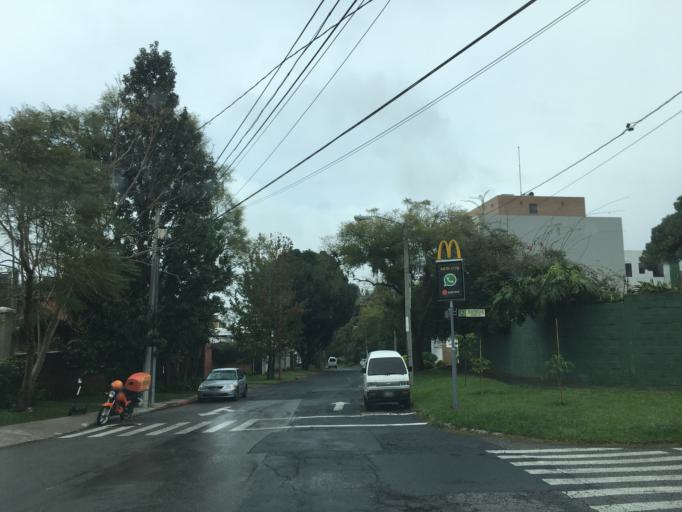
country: GT
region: Guatemala
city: Santa Catarina Pinula
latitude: 14.5884
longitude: -90.4951
